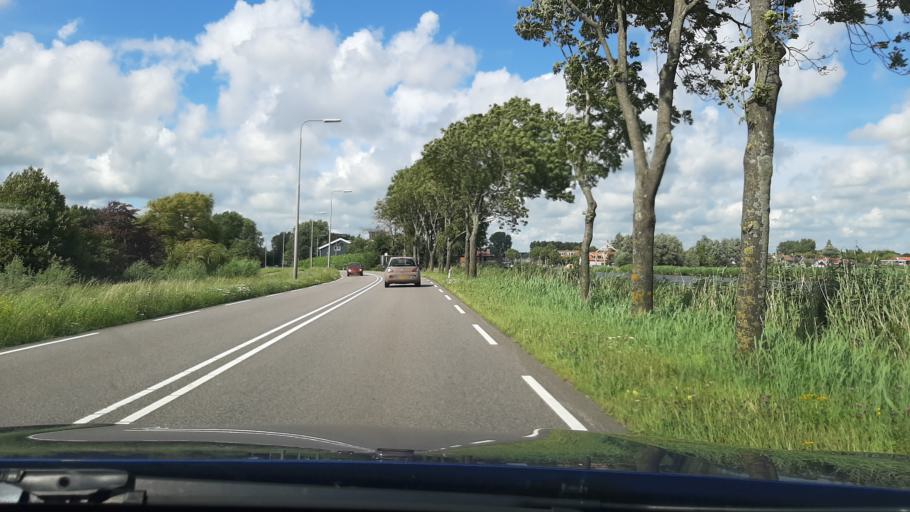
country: NL
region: North Holland
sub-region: Gemeente Zaanstad
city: Zaanstad
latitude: 52.4584
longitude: 4.7615
